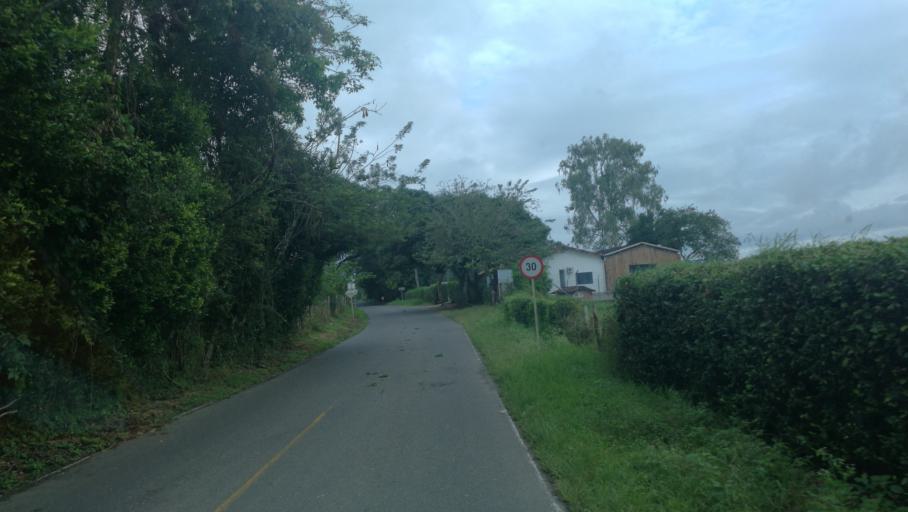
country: CO
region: Quindio
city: Montenegro
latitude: 4.5308
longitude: -75.7738
